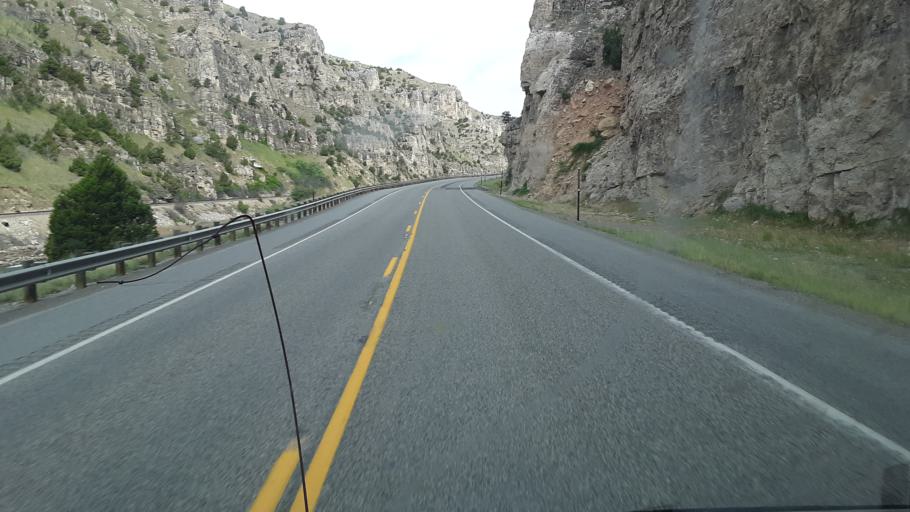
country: US
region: Wyoming
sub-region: Hot Springs County
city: Thermopolis
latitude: 43.5441
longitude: -108.1853
